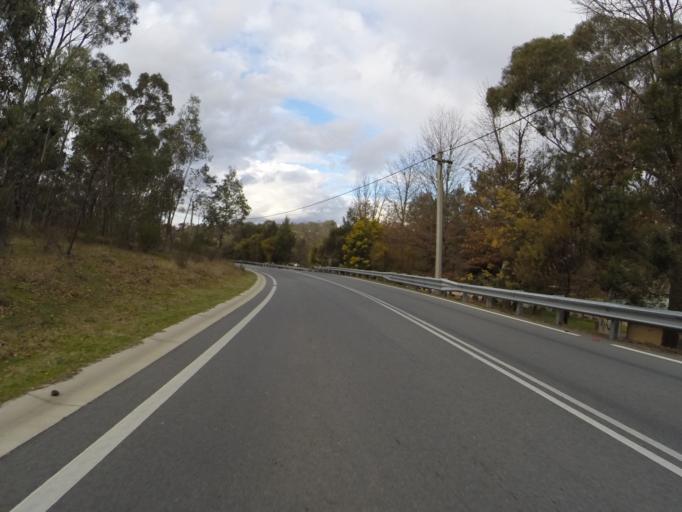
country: AU
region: Australian Capital Territory
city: Macquarie
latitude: -35.3256
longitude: 148.9472
